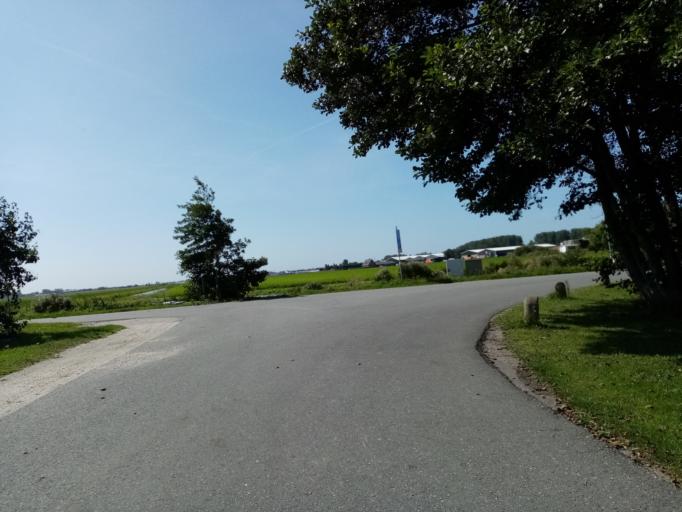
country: NL
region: South Holland
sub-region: Gemeente Noordwijkerhout
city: Noordwijkerhout
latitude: 52.2815
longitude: 4.5243
